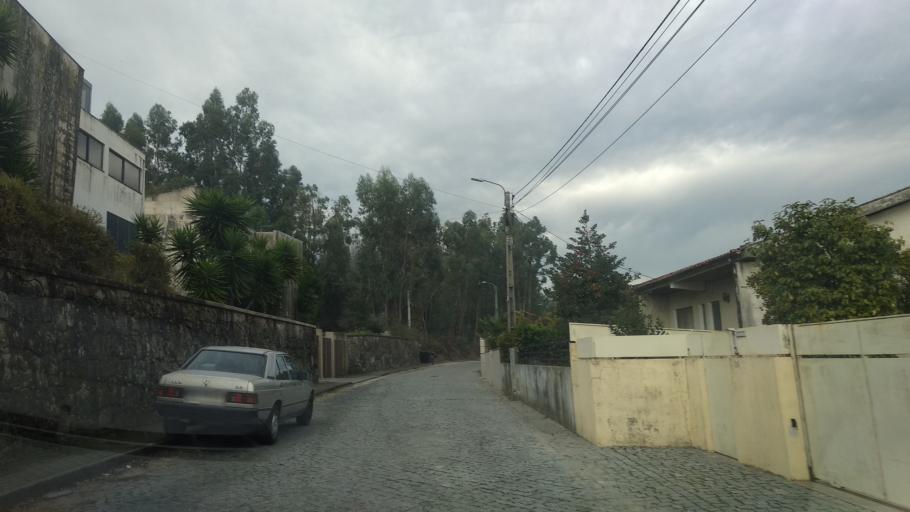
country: PT
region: Braga
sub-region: Braga
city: Braga
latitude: 41.5440
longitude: -8.4613
